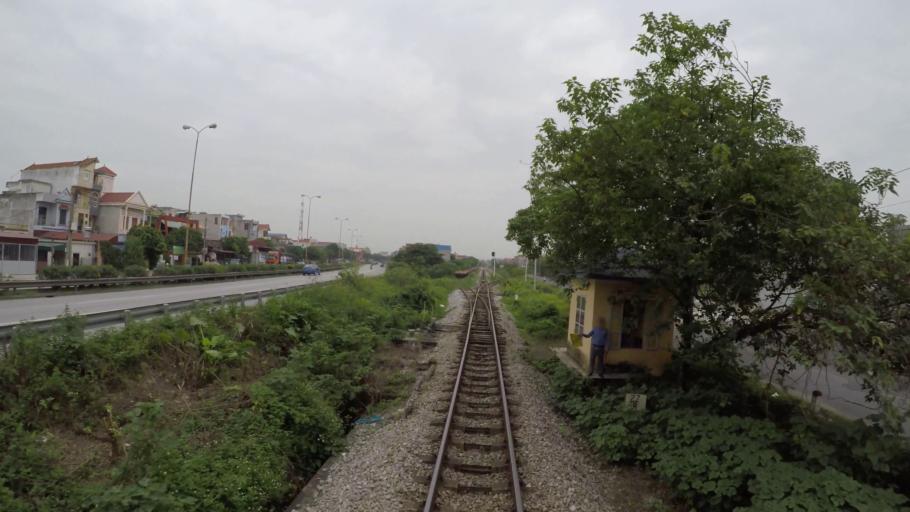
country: VN
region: Hai Duong
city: Phu Thai
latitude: 20.9727
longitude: 106.4778
